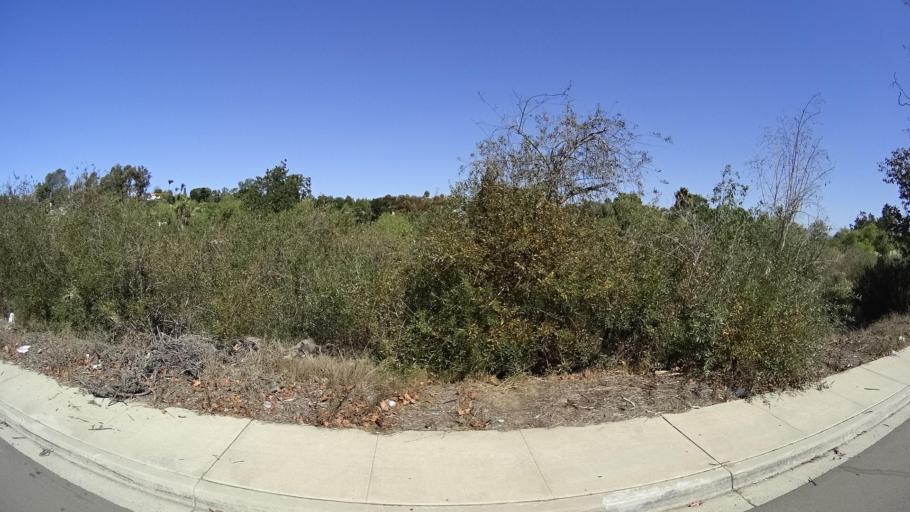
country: US
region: California
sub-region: San Diego County
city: Chula Vista
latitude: 32.6494
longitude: -117.0609
